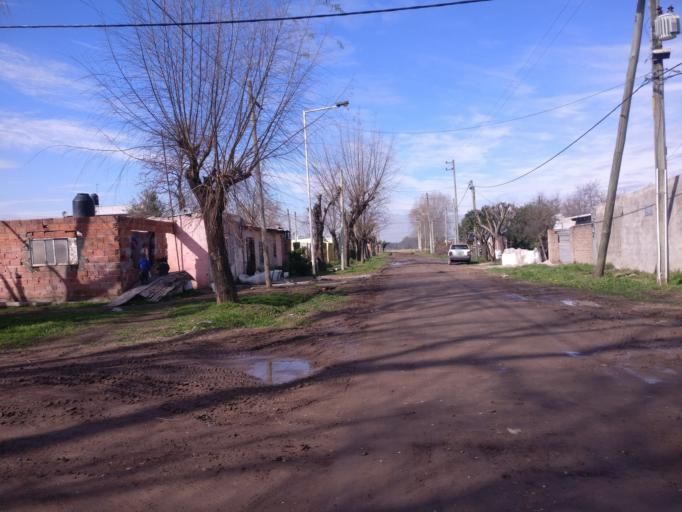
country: AR
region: Buenos Aires
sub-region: Partido de Ezeiza
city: Ezeiza
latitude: -34.9421
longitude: -58.6073
